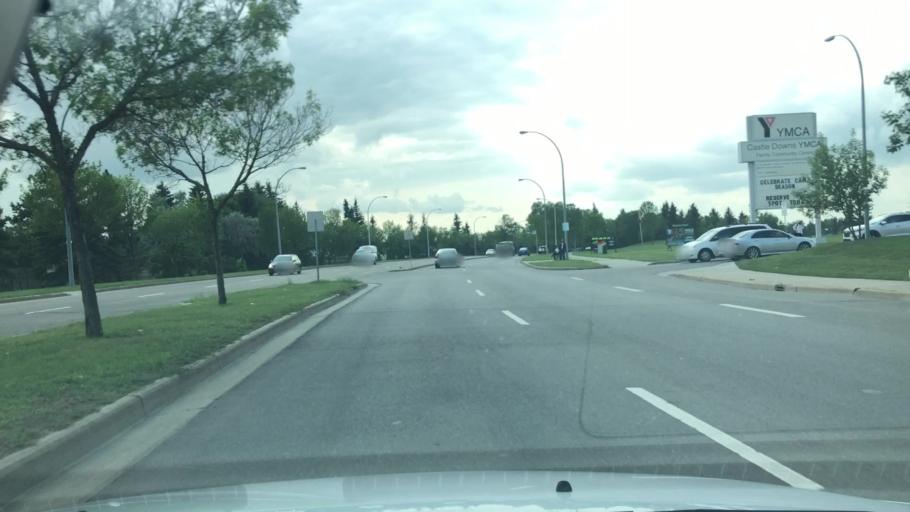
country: CA
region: Alberta
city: Edmonton
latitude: 53.6142
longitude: -113.5198
